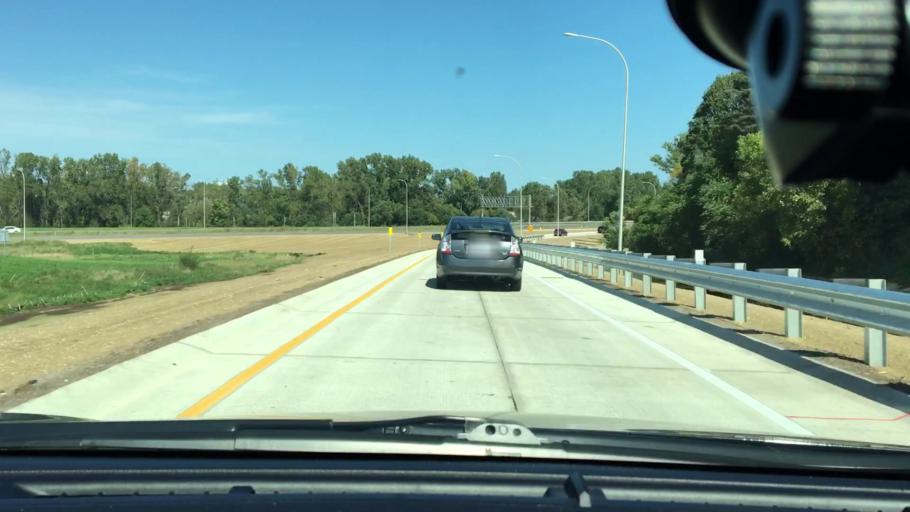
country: US
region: Minnesota
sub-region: Ramsey County
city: Little Canada
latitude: 45.0092
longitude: -93.0882
